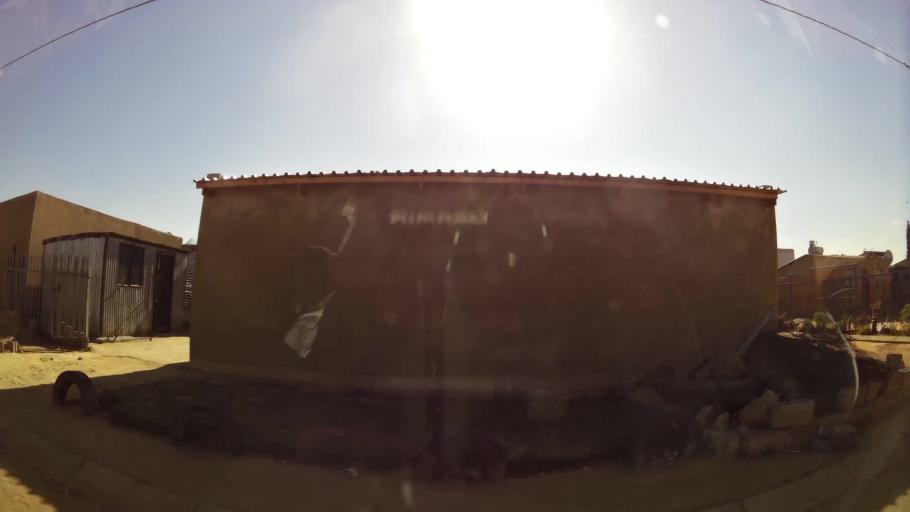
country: ZA
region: Gauteng
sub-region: Ekurhuleni Metropolitan Municipality
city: Tembisa
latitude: -26.0256
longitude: 28.2401
